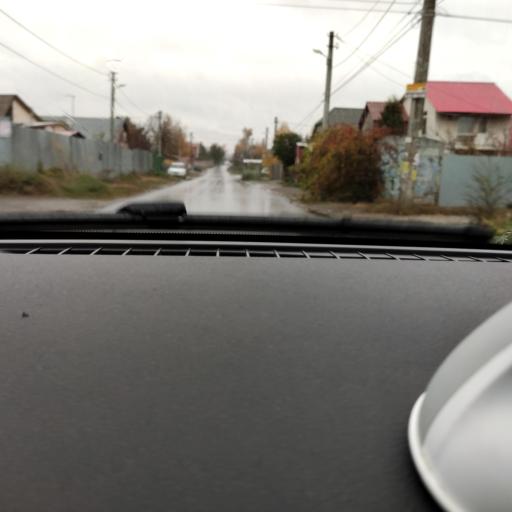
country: RU
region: Samara
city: Samara
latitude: 53.2303
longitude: 50.2290
